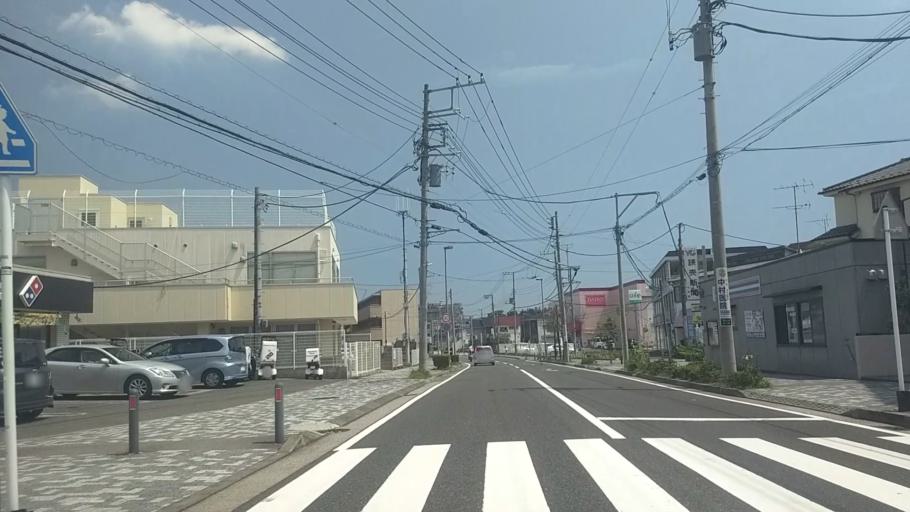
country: JP
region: Kanagawa
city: Yokohama
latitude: 35.4872
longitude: 139.6131
